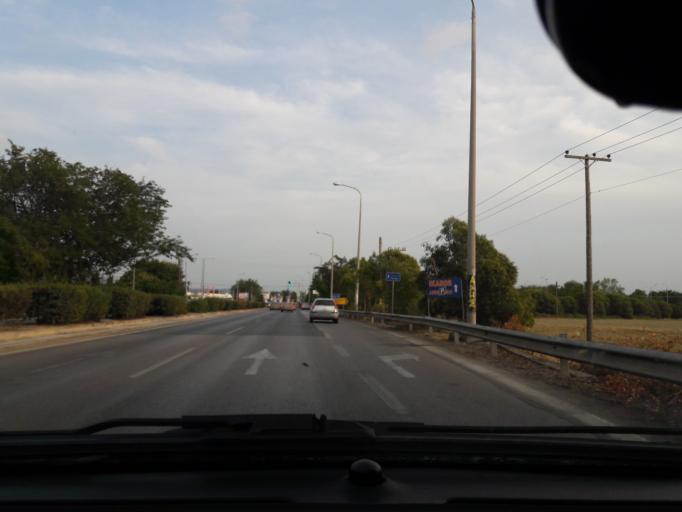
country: GR
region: Central Macedonia
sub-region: Nomos Thessalonikis
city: Thermi
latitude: 40.5342
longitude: 22.9932
